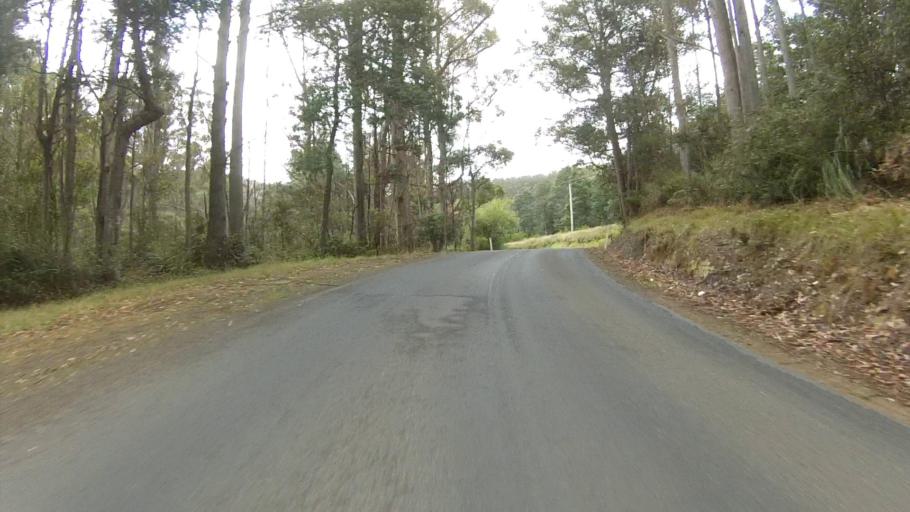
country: AU
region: Tasmania
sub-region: Huon Valley
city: Cygnet
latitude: -43.1451
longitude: 147.1534
